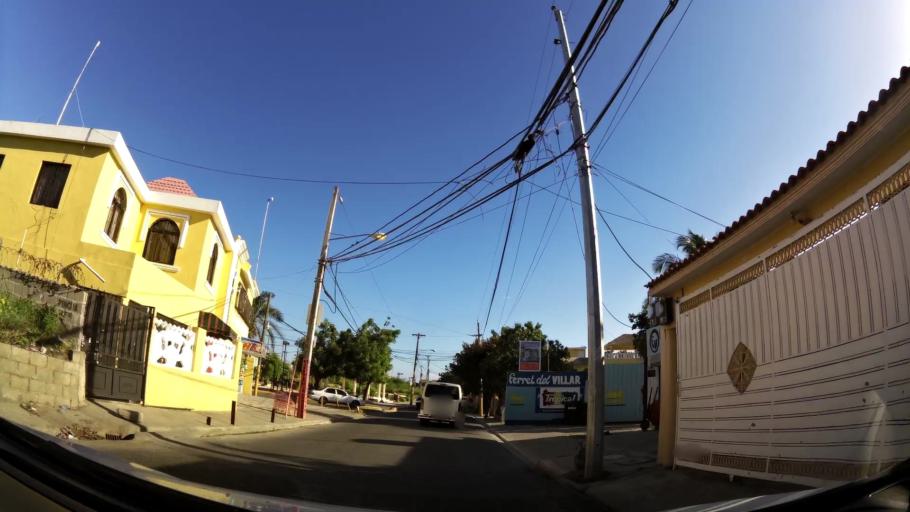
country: DO
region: Santo Domingo
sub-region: Santo Domingo
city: Santo Domingo Este
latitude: 18.4914
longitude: -69.8063
